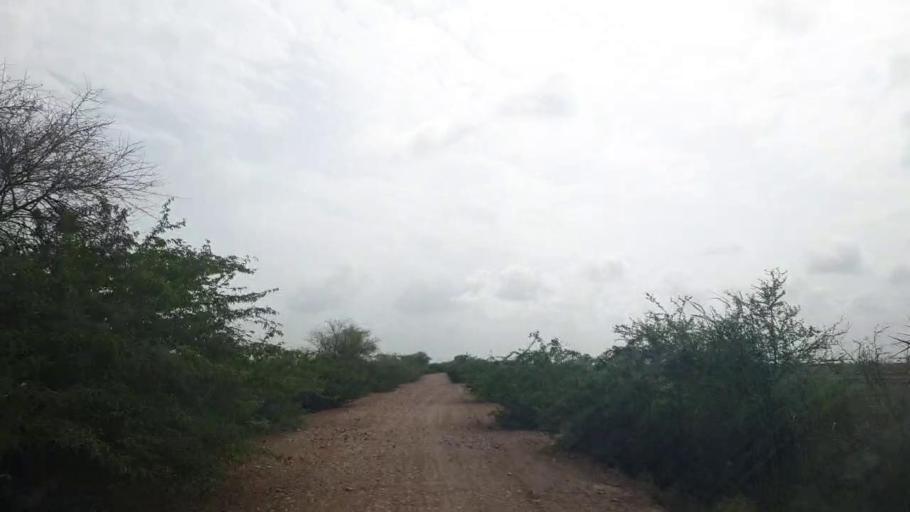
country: PK
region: Sindh
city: Tando Bago
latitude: 24.8180
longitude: 69.0492
